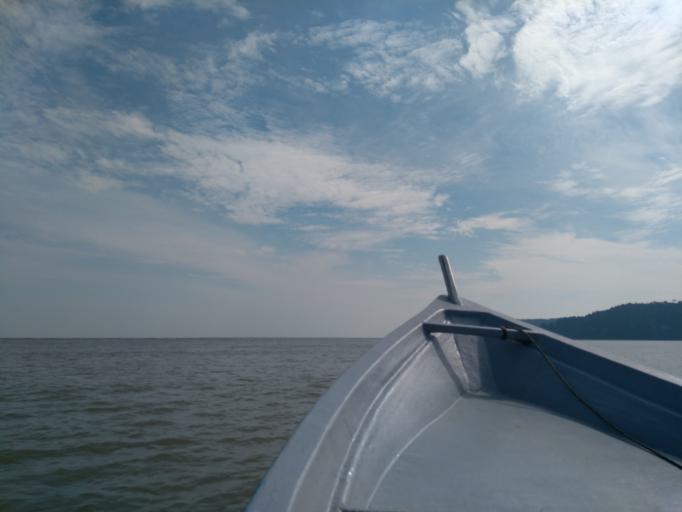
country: MY
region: Sarawak
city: Kuching
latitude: 1.7044
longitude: 110.4303
